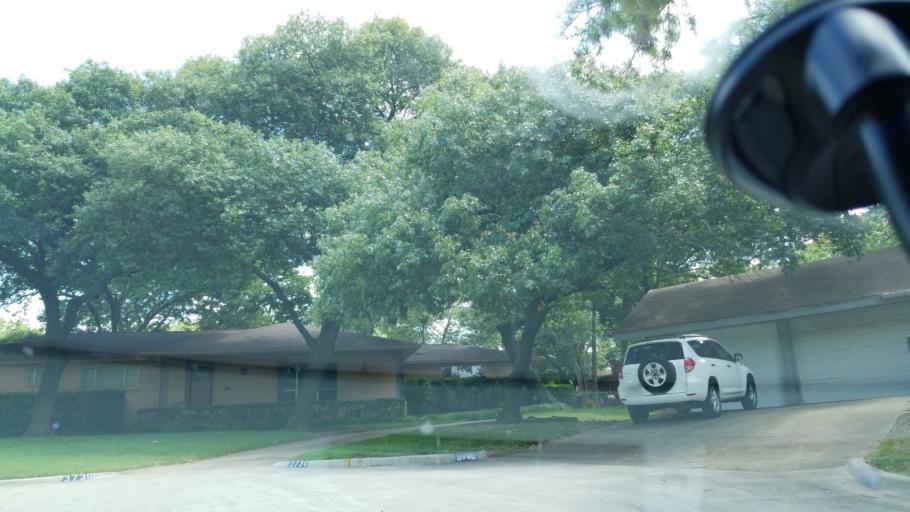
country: US
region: Texas
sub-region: Dallas County
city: Cockrell Hill
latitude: 32.6971
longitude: -96.8548
